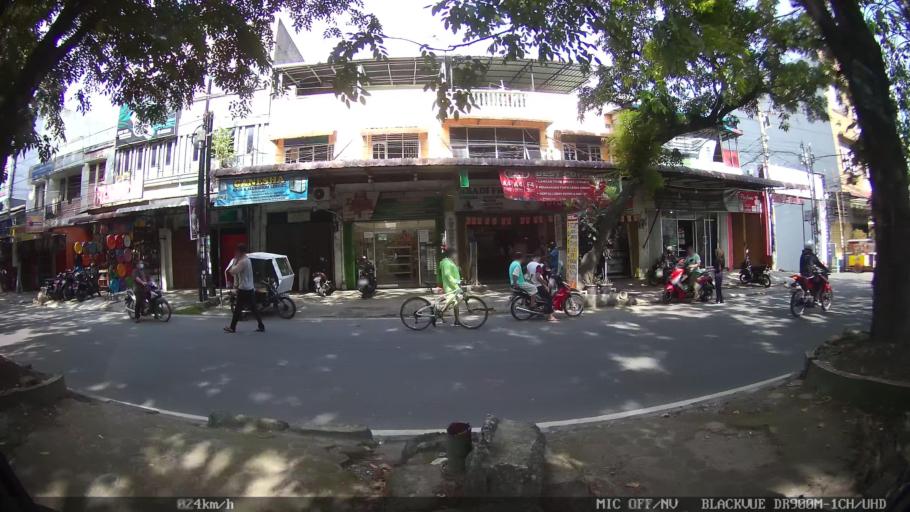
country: ID
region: North Sumatra
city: Medan
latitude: 3.5734
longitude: 98.6426
